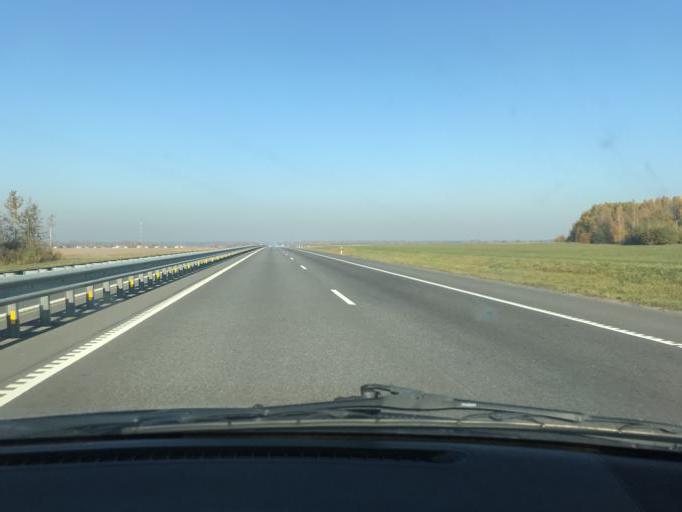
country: BY
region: Minsk
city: Slutsk
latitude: 53.2037
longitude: 27.5509
